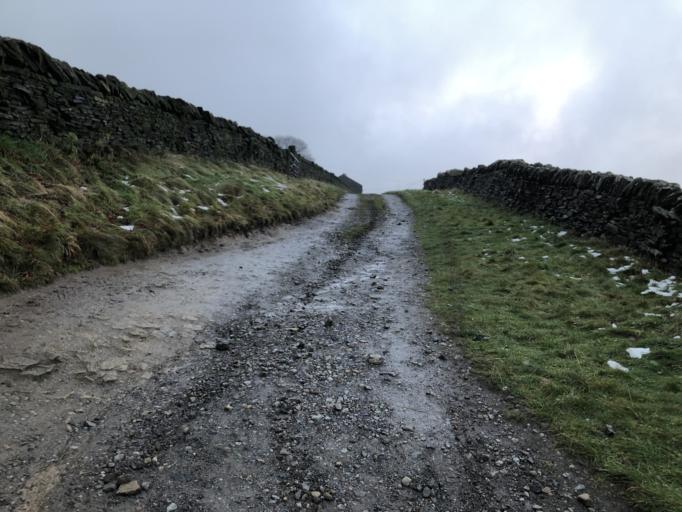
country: GB
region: England
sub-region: Kirklees
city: Holmfirth
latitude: 53.5483
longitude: -1.7955
